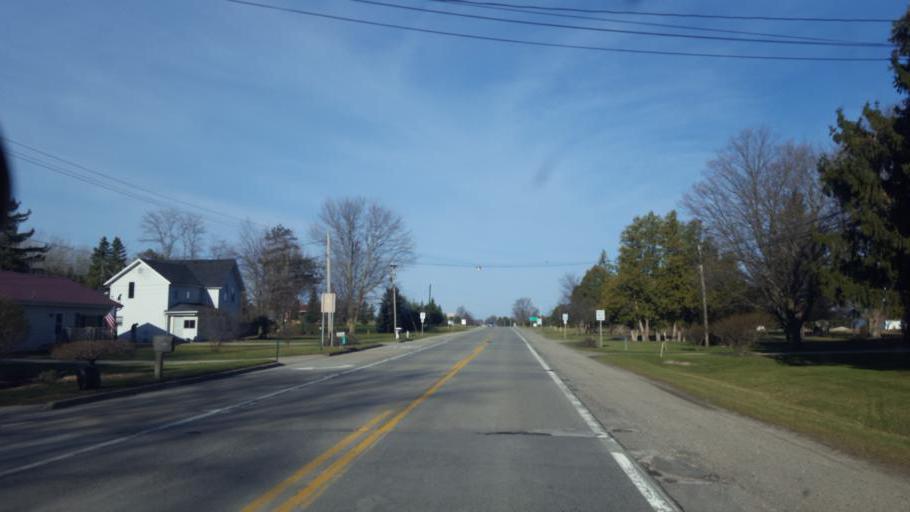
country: US
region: Michigan
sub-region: Montcalm County
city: Edmore
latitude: 43.4082
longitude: -85.0512
